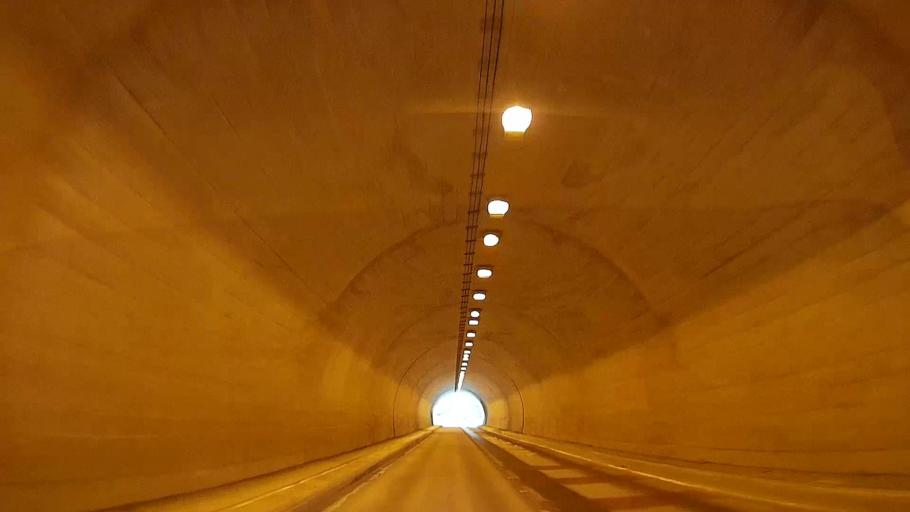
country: JP
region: Saitama
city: Chichibu
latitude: 35.9549
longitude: 139.0557
